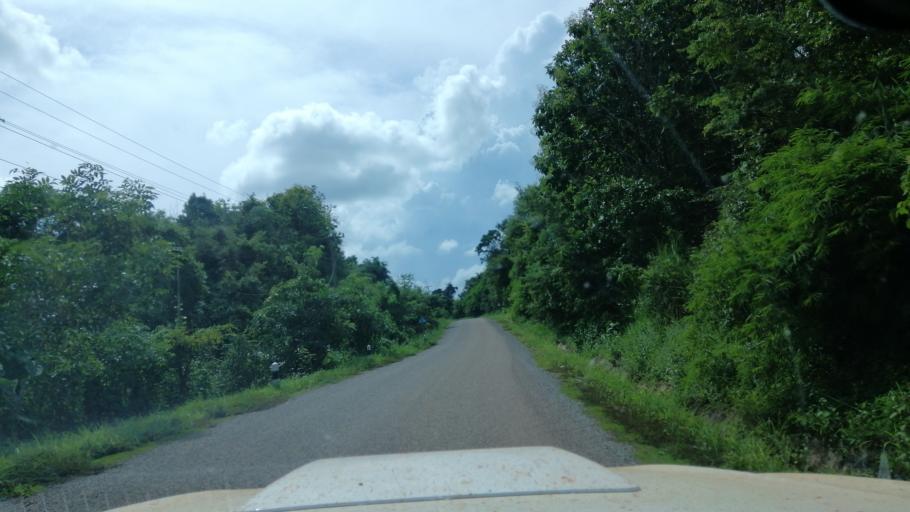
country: TH
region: Nan
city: Mae Charim
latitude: 18.3953
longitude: 101.1722
